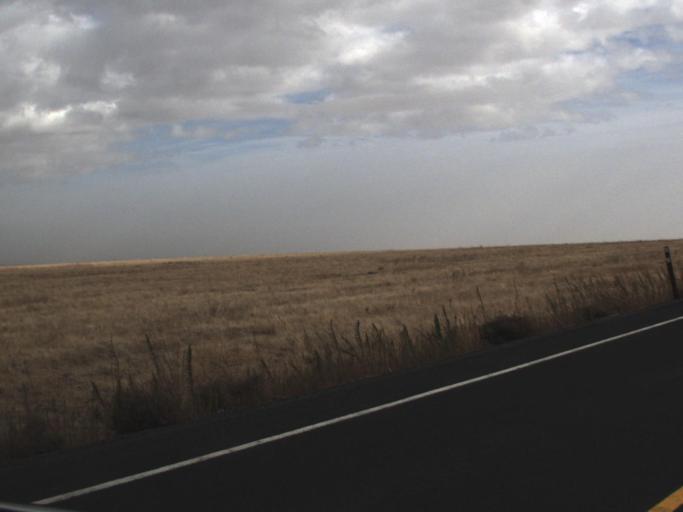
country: US
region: Washington
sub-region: Adams County
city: Ritzville
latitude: 47.4529
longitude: -118.7466
